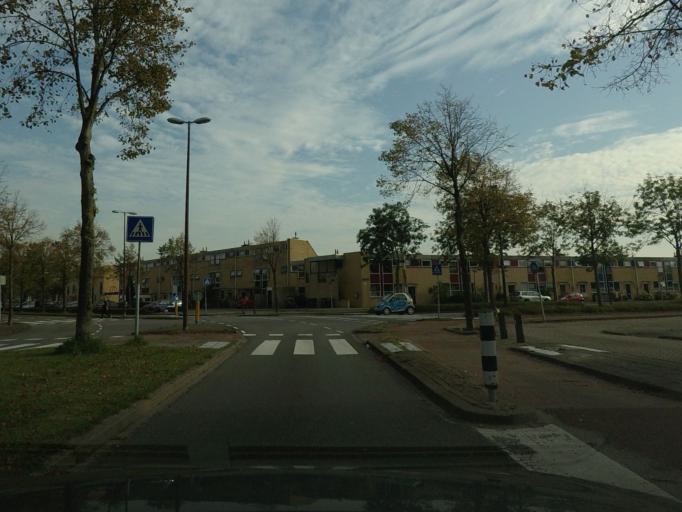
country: NL
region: North Holland
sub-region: Gemeente Alkmaar
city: Alkmaar
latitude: 52.6674
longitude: 4.7607
